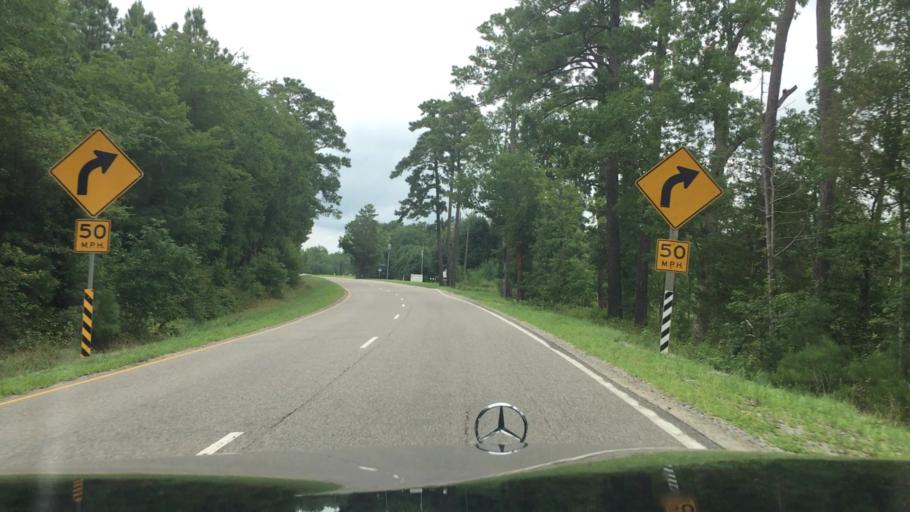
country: US
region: Virginia
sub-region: Chesterfield County
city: Woodlake
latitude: 37.3847
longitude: -77.8003
